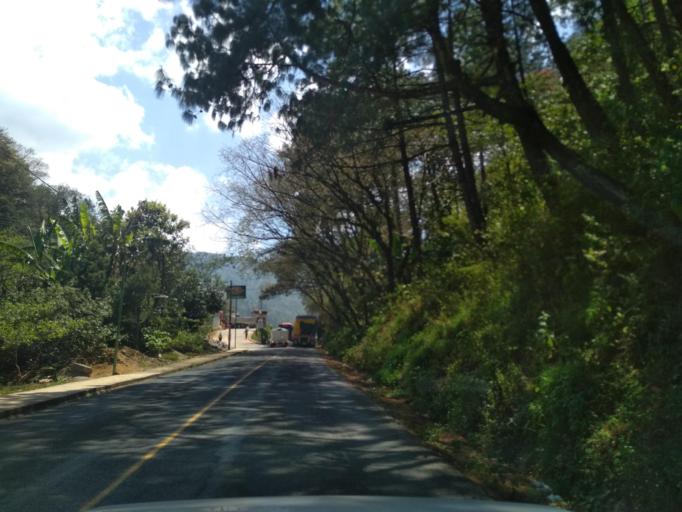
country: MX
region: Veracruz
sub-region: Tlilapan
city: Tonalixco
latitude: 18.7779
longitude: -97.0833
